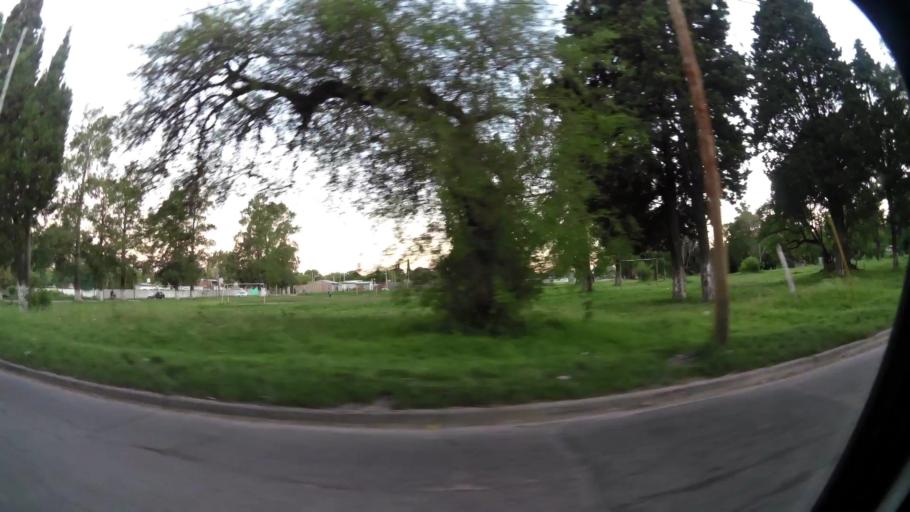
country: AR
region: Buenos Aires
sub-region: Partido de Quilmes
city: Quilmes
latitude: -34.7995
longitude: -58.1904
